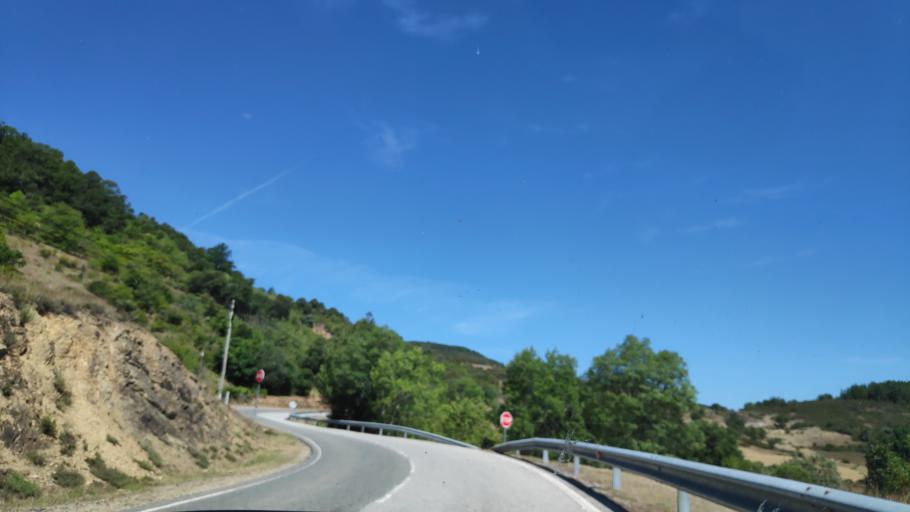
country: PT
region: Braganca
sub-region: Braganca Municipality
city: Braganca
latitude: 41.8961
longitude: -6.7282
